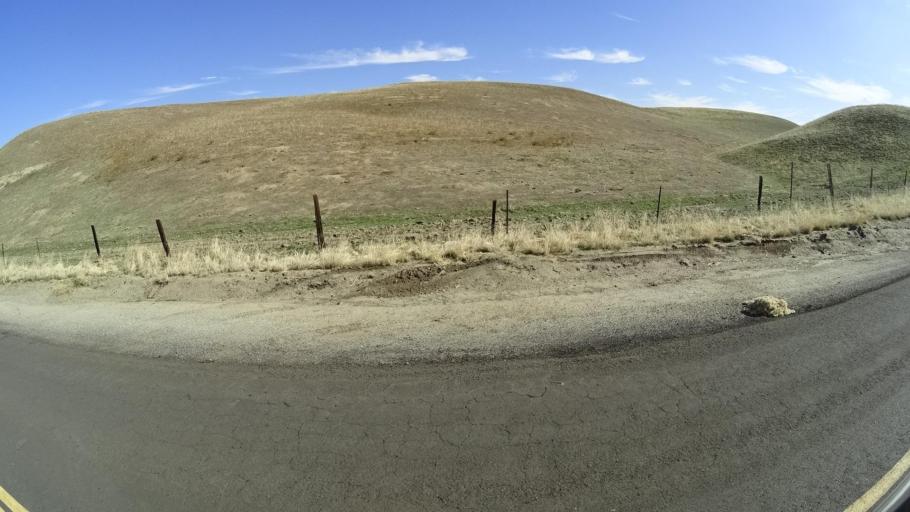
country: US
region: California
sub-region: Tulare County
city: Richgrove
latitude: 35.6429
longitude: -118.9425
